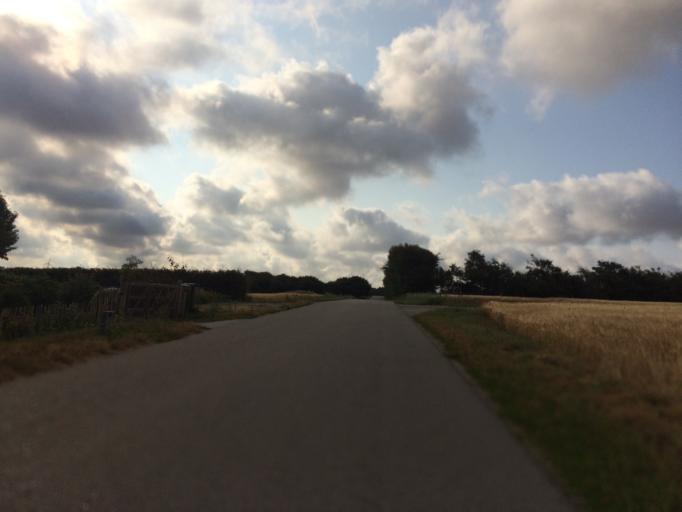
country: DK
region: Central Jutland
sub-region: Holstebro Kommune
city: Vinderup
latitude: 56.6096
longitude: 8.7826
